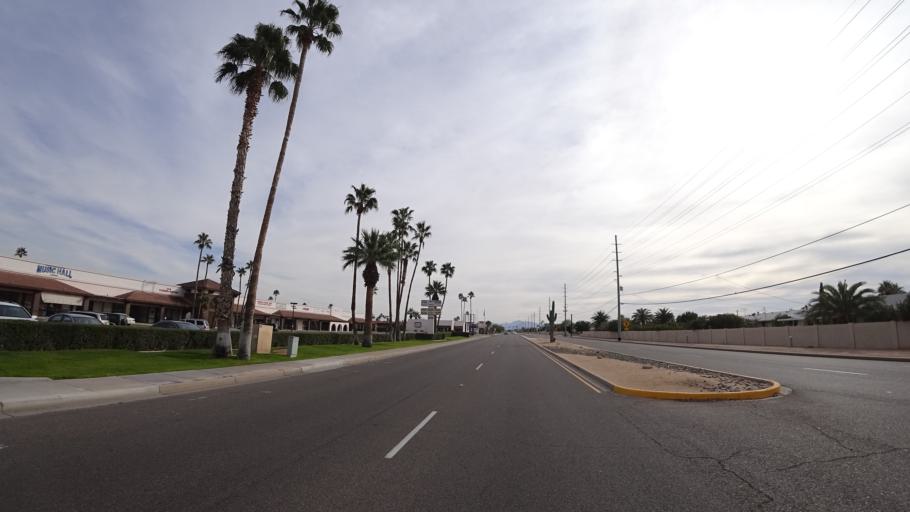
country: US
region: Arizona
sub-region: Maricopa County
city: Sun City
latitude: 33.5838
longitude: -112.2725
